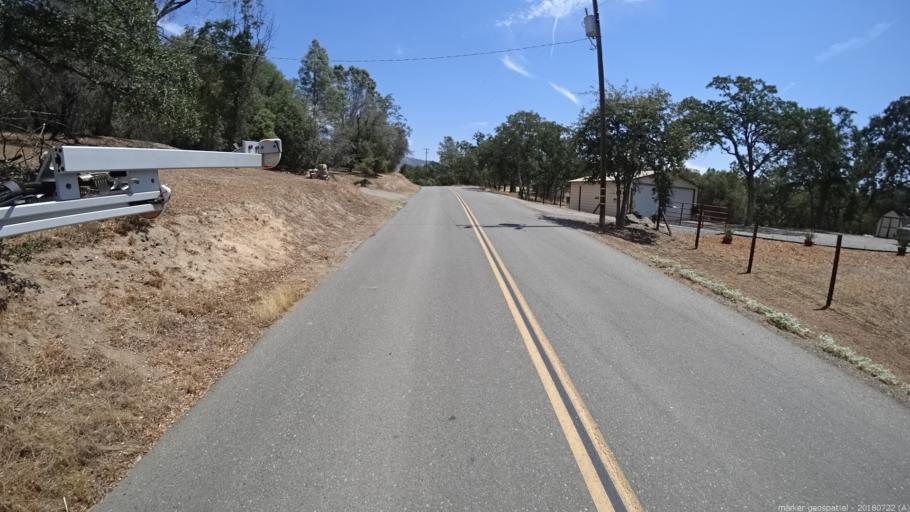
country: US
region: California
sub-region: Madera County
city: Coarsegold
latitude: 37.2704
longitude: -119.7488
